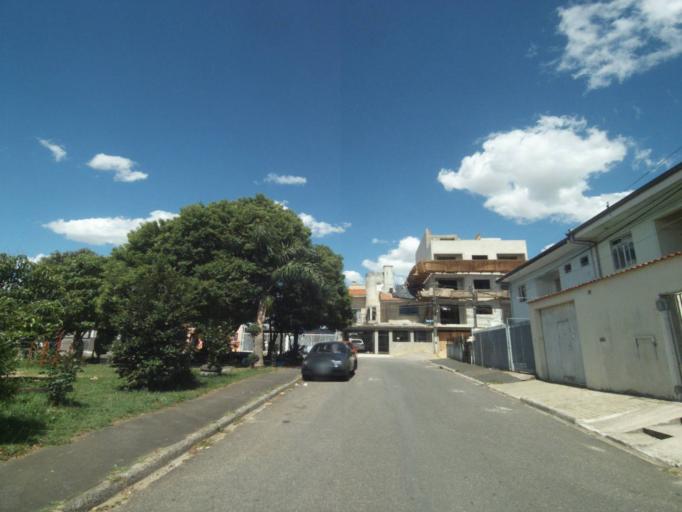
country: BR
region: Parana
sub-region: Curitiba
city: Curitiba
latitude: -25.5106
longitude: -49.3246
